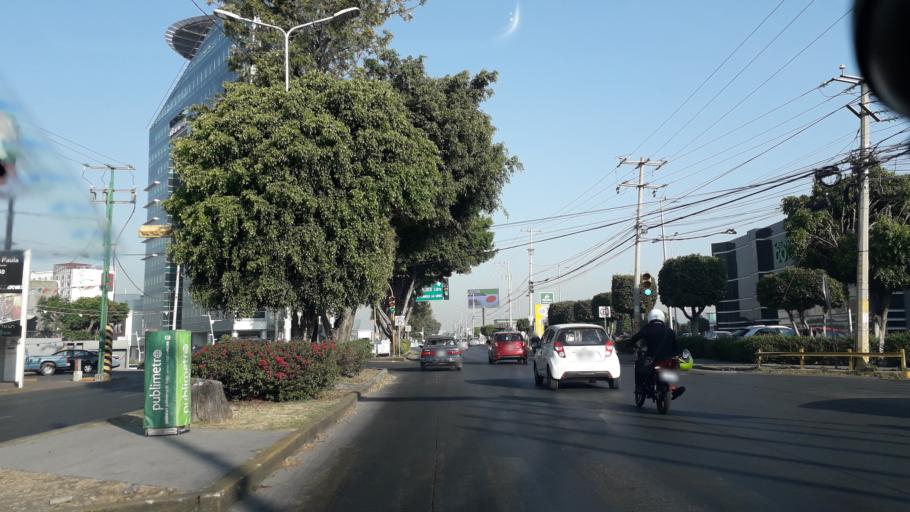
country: MX
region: Puebla
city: Puebla
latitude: 19.0430
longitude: -98.2328
